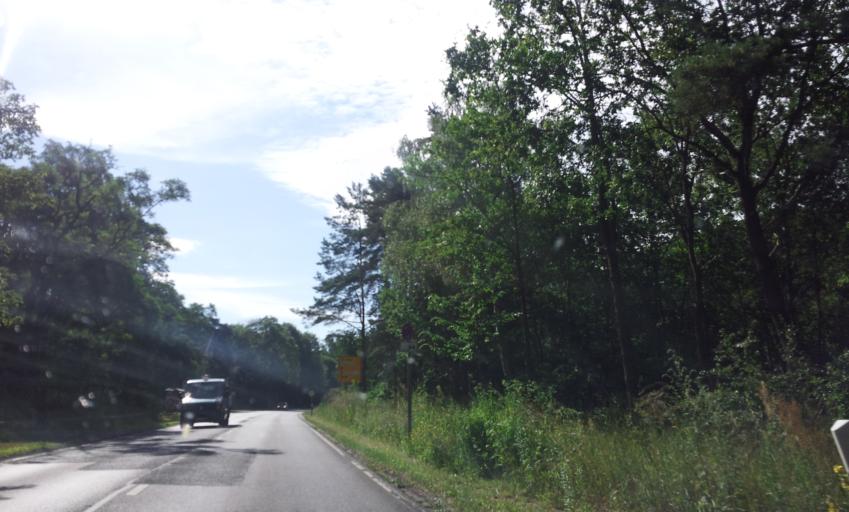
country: DE
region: Berlin
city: Friedrichshagen
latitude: 52.4307
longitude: 13.6132
